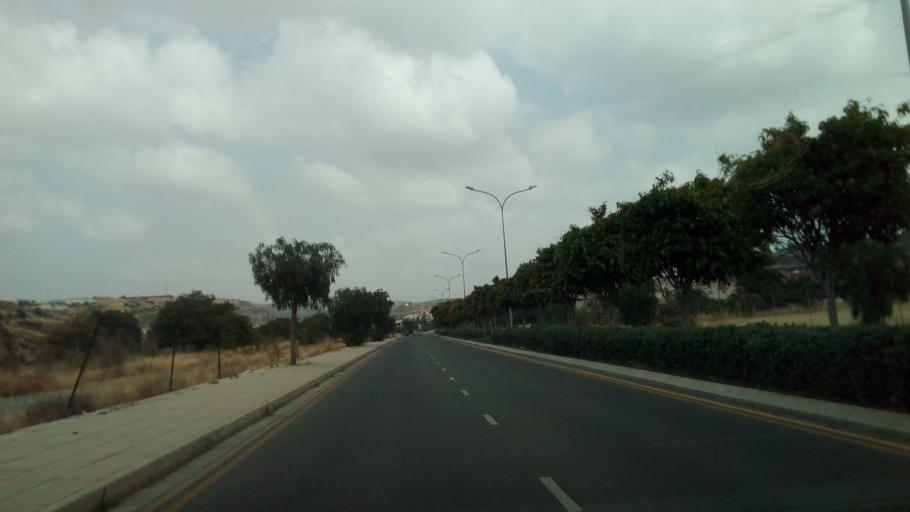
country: CY
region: Limassol
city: Pano Polemidia
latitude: 34.7074
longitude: 33.0014
